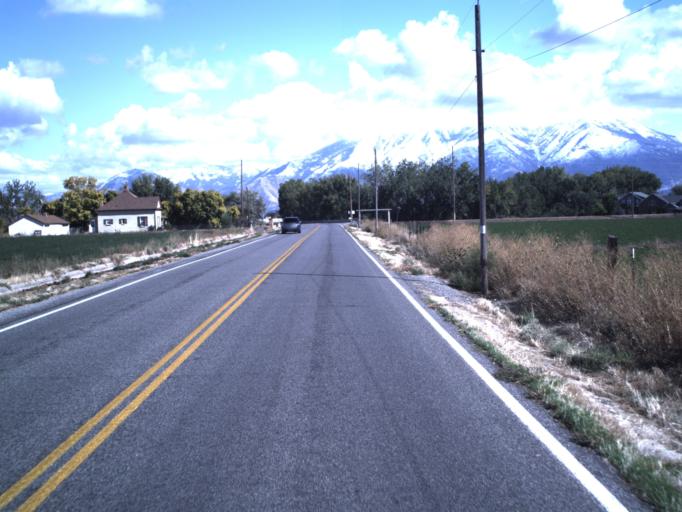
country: US
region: Utah
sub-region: Utah County
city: Benjamin
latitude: 40.1148
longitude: -111.7011
